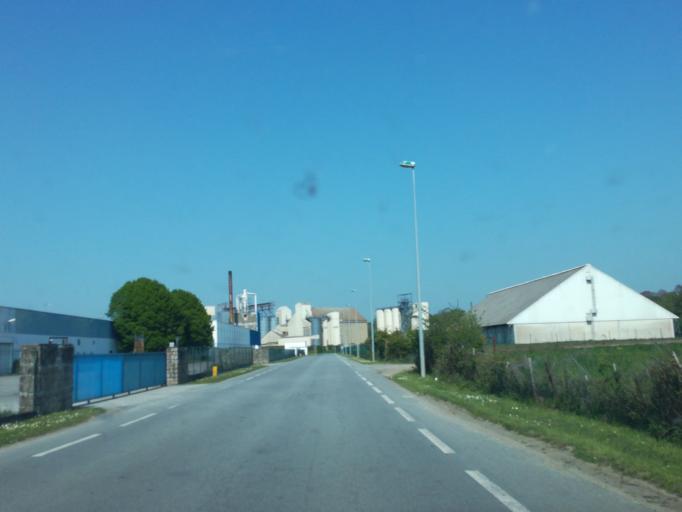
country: FR
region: Brittany
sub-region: Departement du Morbihan
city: Le Sourn
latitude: 48.0446
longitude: -2.9634
